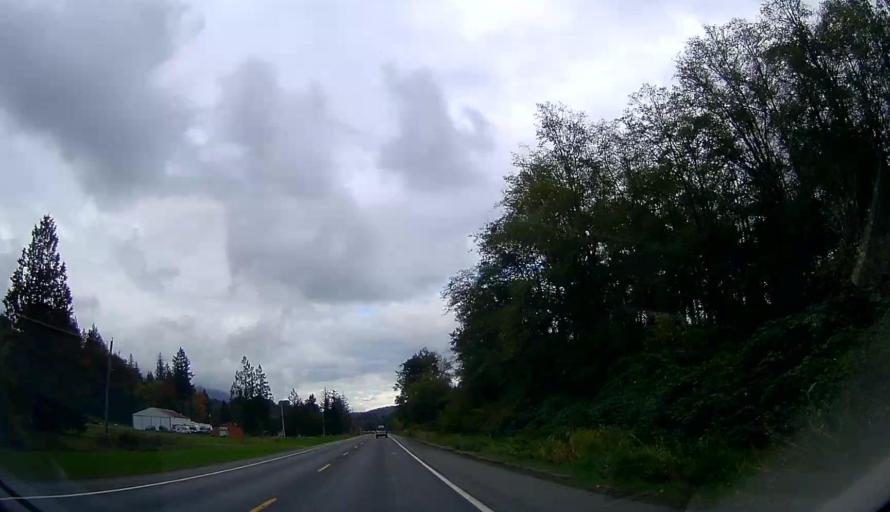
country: US
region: Washington
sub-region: Skagit County
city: Sedro-Woolley
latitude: 48.5269
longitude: -122.1705
